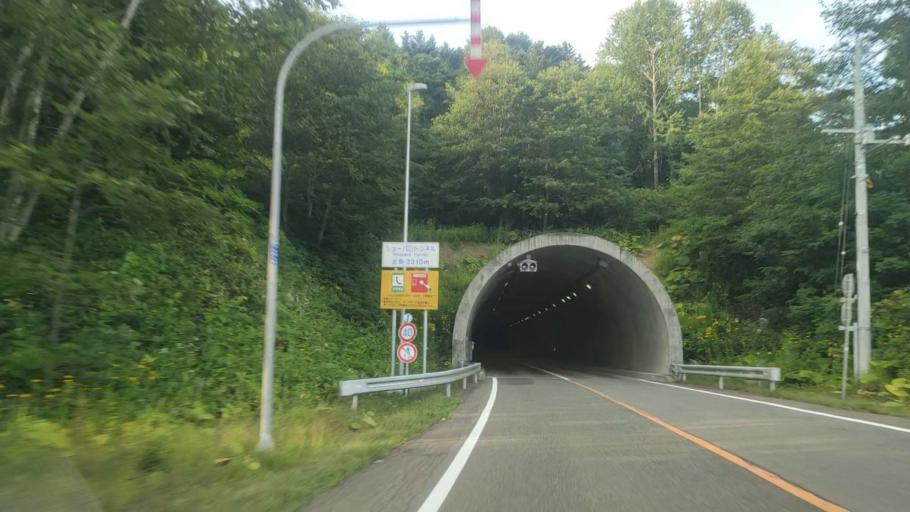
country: JP
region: Hokkaido
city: Iwamizawa
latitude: 43.0243
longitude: 142.0860
